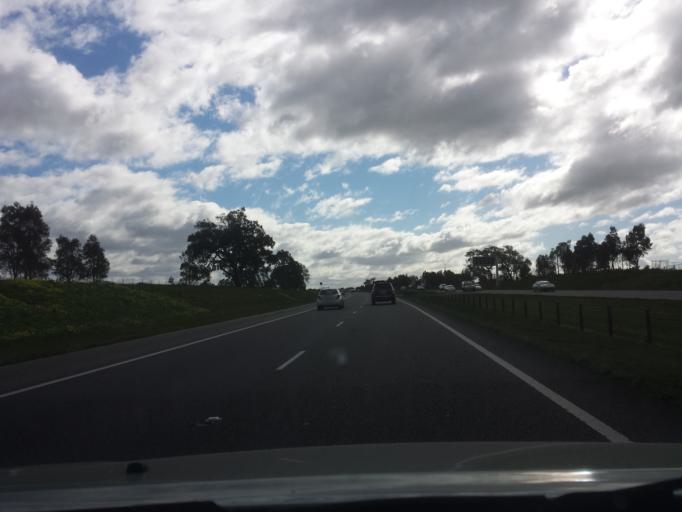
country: AU
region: Victoria
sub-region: Hume
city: Craigieburn
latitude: -37.6202
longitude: 144.9914
